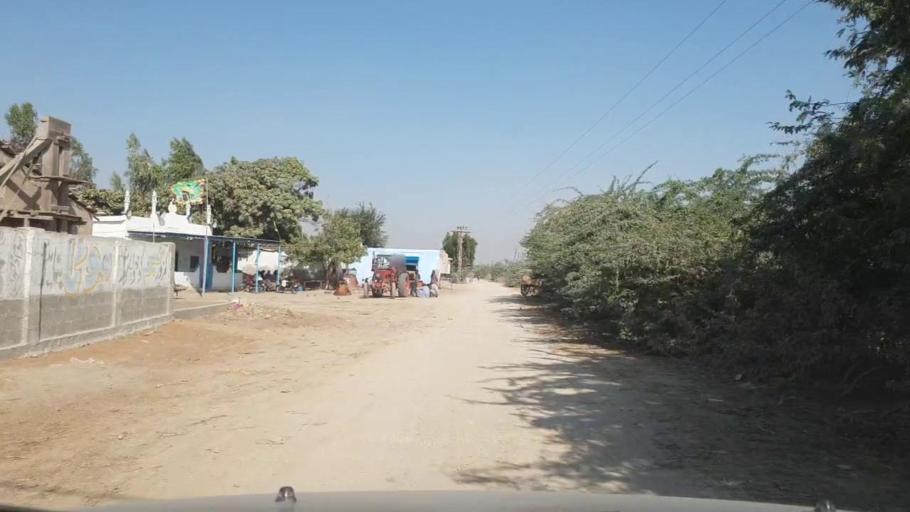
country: PK
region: Sindh
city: Thatta
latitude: 24.8000
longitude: 67.9020
